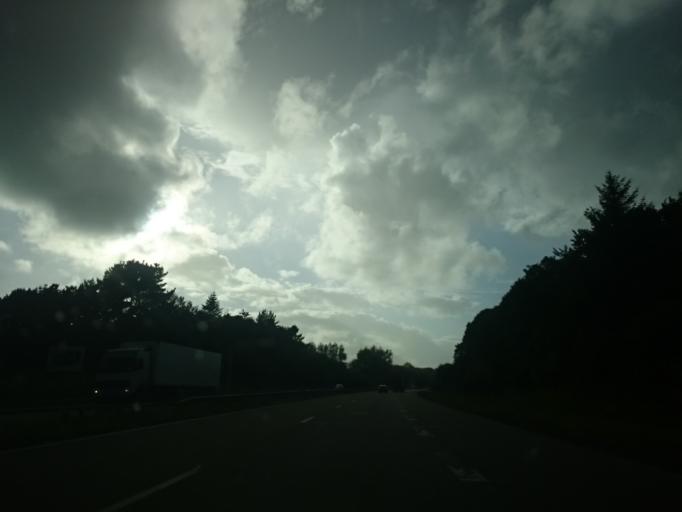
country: FR
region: Brittany
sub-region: Departement du Finistere
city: Plouigneau
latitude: 48.5754
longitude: -3.7222
